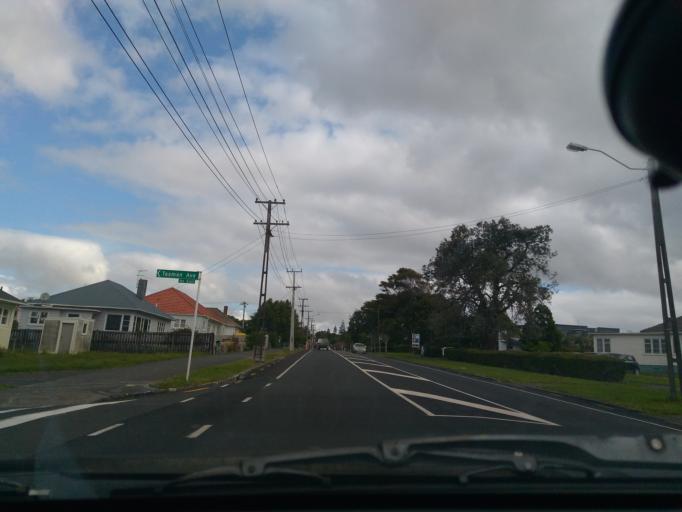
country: NZ
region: Auckland
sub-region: Auckland
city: Rosebank
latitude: -36.8761
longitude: 174.7105
